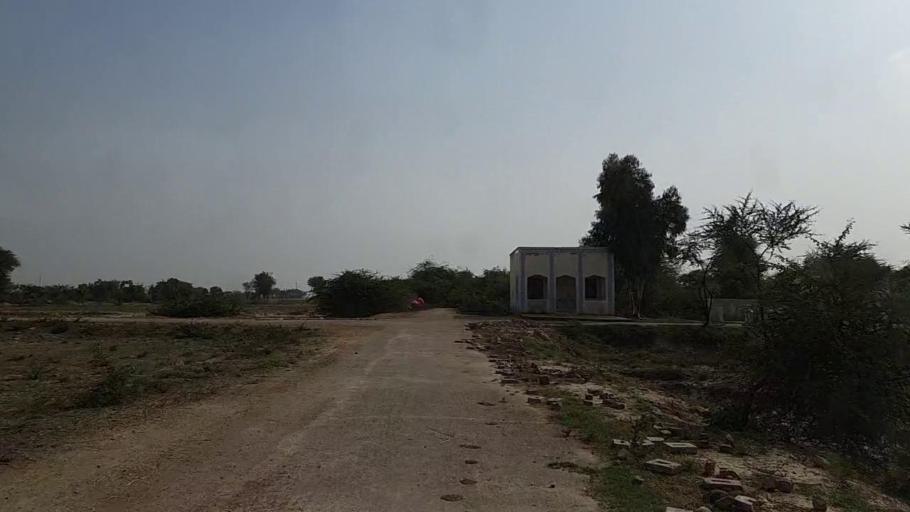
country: PK
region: Sindh
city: Naukot
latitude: 24.7569
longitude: 69.3144
